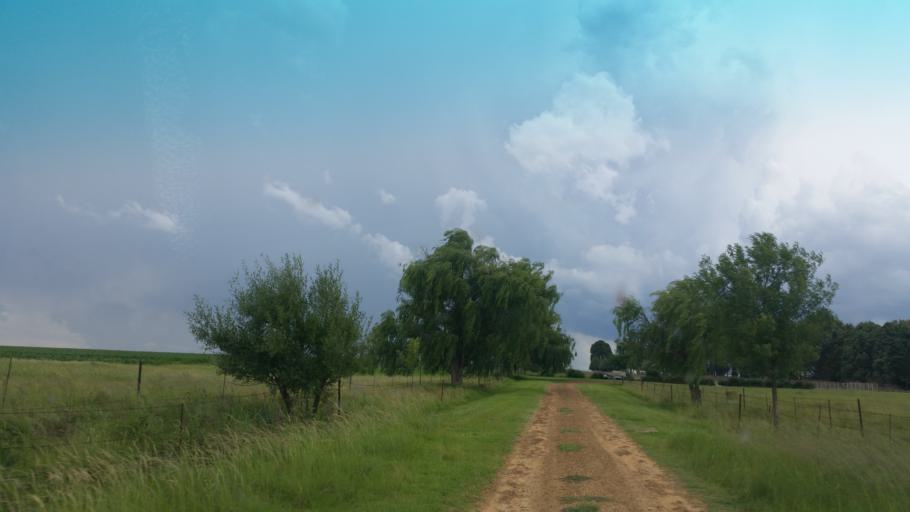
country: ZA
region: Orange Free State
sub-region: Thabo Mofutsanyana District Municipality
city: Harrismith
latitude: -28.1913
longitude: 29.0163
